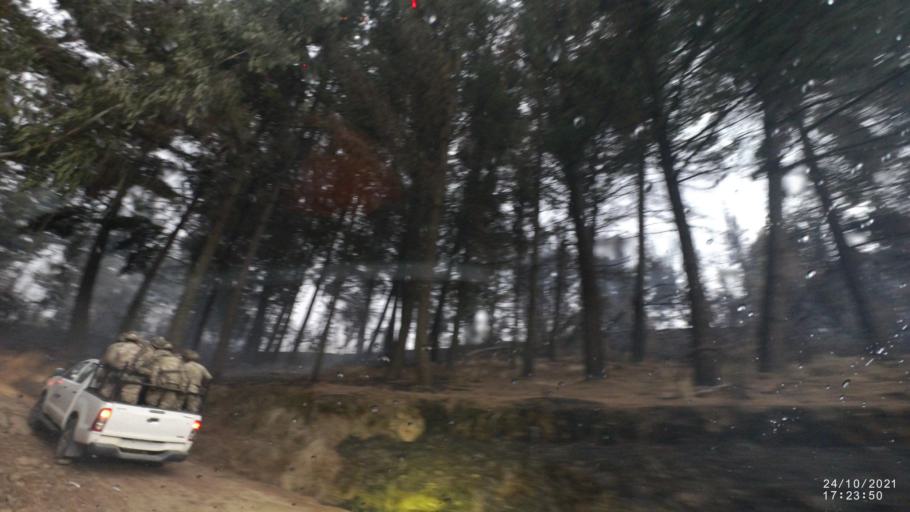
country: BO
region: Cochabamba
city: Cochabamba
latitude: -17.3262
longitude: -66.1341
